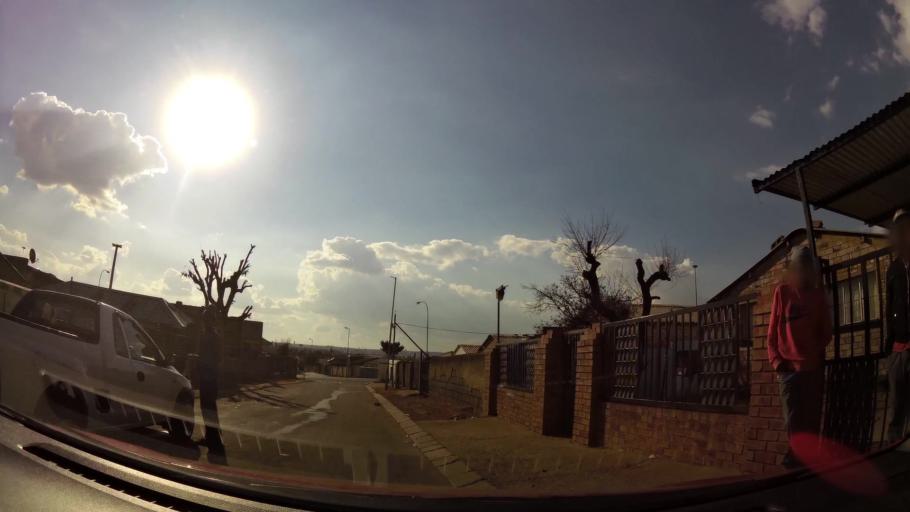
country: ZA
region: Gauteng
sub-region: City of Johannesburg Metropolitan Municipality
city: Soweto
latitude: -26.2310
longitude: 27.8695
